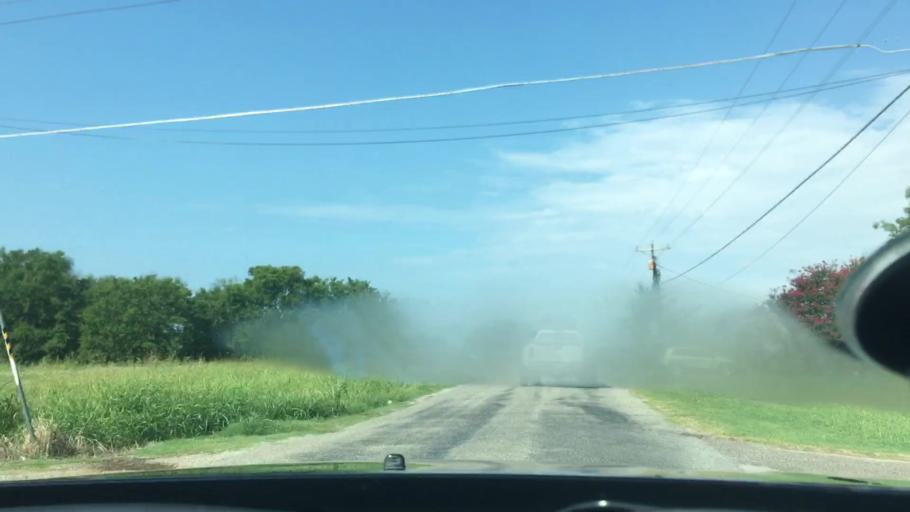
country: US
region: Oklahoma
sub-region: Bryan County
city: Colbert
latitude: 33.9110
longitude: -96.5354
